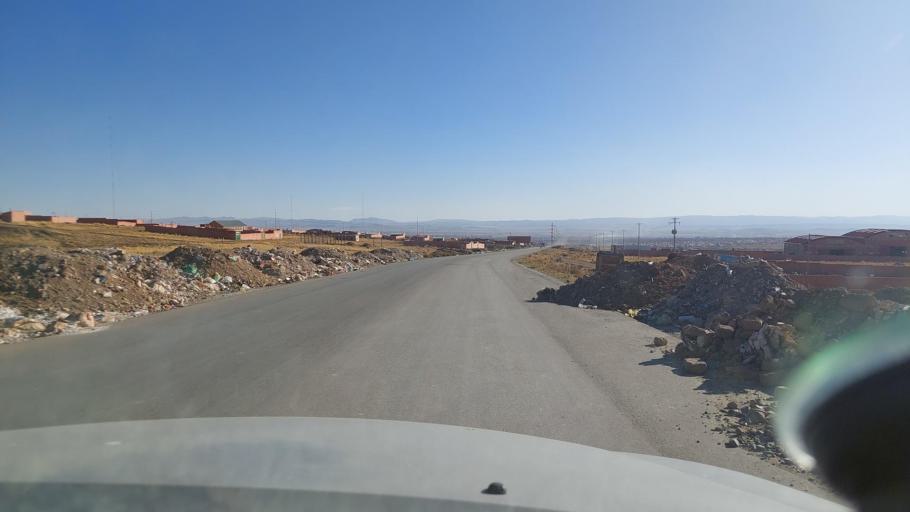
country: BO
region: La Paz
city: La Paz
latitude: -16.4399
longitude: -68.1645
